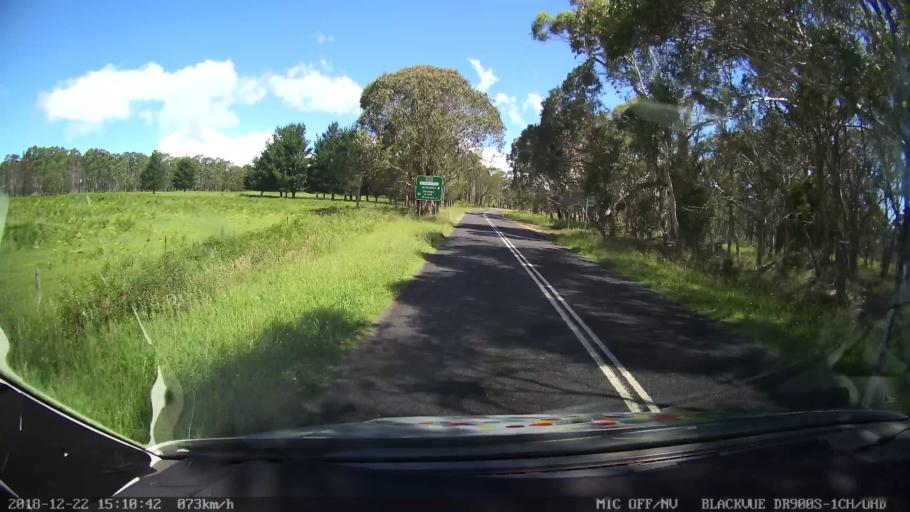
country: AU
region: New South Wales
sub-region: Bellingen
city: Dorrigo
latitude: -30.3377
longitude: 152.4064
